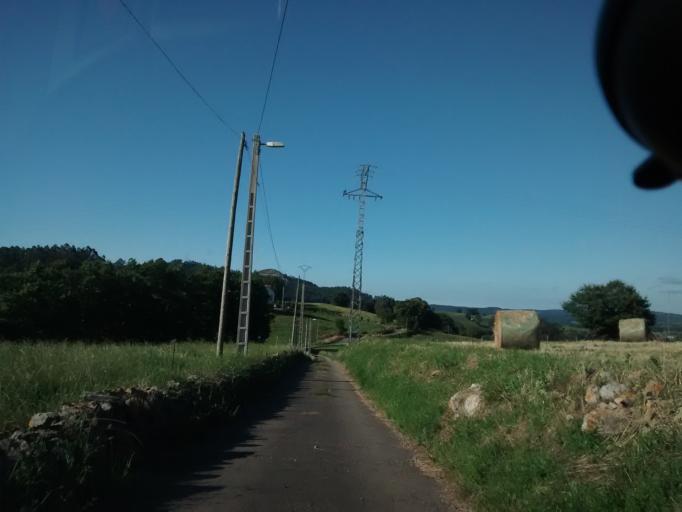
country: ES
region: Cantabria
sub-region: Provincia de Cantabria
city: Entrambasaguas
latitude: 43.3628
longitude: -3.7077
